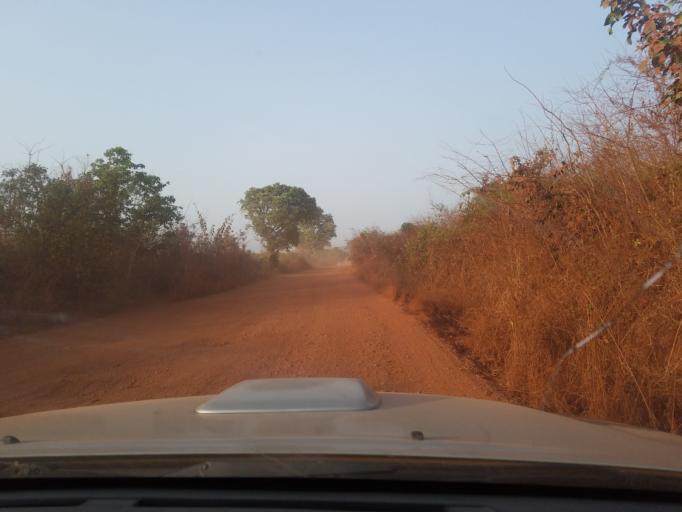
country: GN
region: Boke
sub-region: Gaoual Prefecture
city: Gaoual
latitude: 11.5052
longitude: -13.8598
